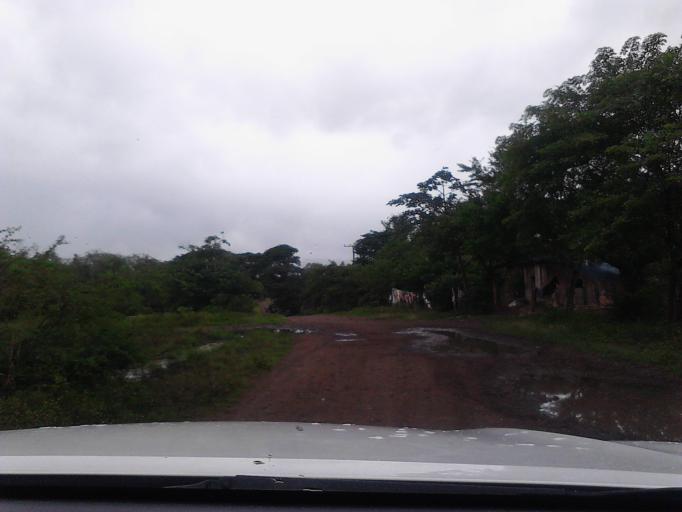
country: NI
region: Matagalpa
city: Ciudad Dario
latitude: 12.9008
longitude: -86.1384
